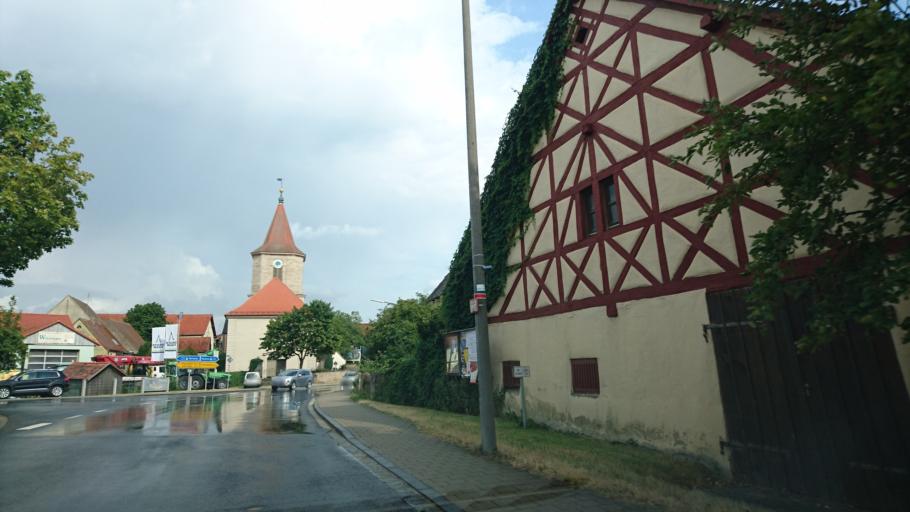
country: DE
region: Bavaria
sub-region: Regierungsbezirk Mittelfranken
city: Thalmassing
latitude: 49.1075
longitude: 11.1859
